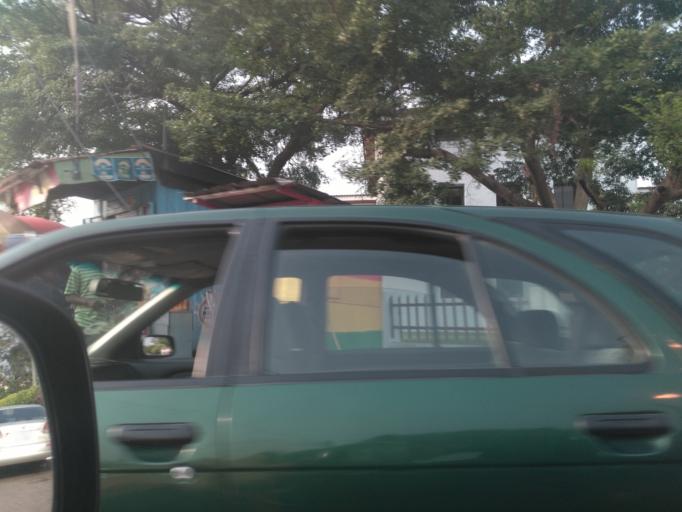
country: GH
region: Greater Accra
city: Accra
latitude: 5.6062
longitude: -0.1972
